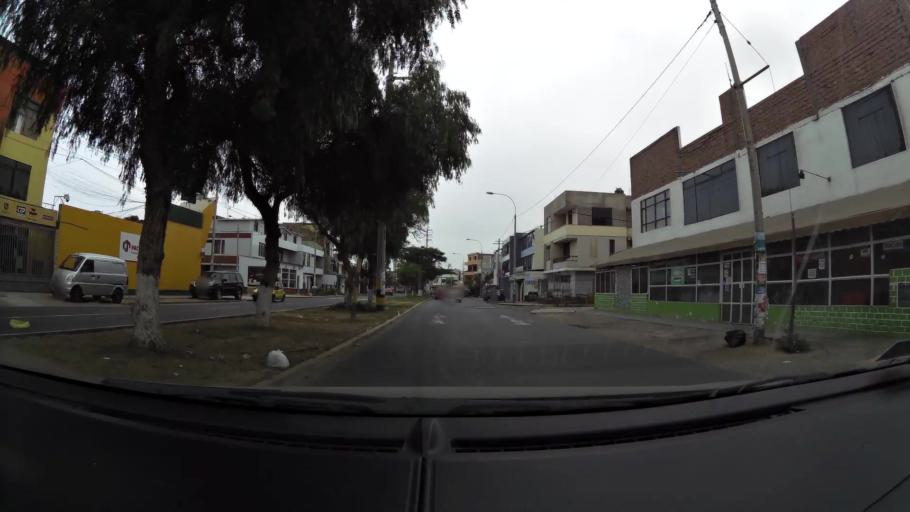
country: PE
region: La Libertad
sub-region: Provincia de Trujillo
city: Trujillo
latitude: -8.0978
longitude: -79.0300
